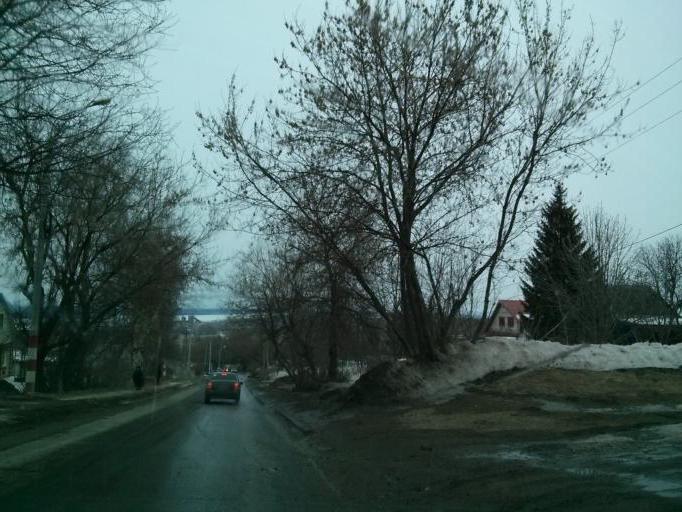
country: RU
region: Nizjnij Novgorod
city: Afonino
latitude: 56.2952
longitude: 44.0899
